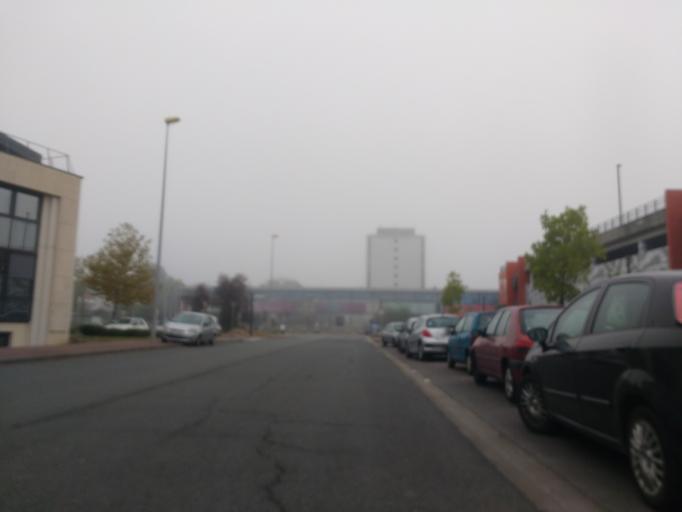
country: FR
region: Aquitaine
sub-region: Departement de la Gironde
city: Talence
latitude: 44.8054
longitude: -0.6013
